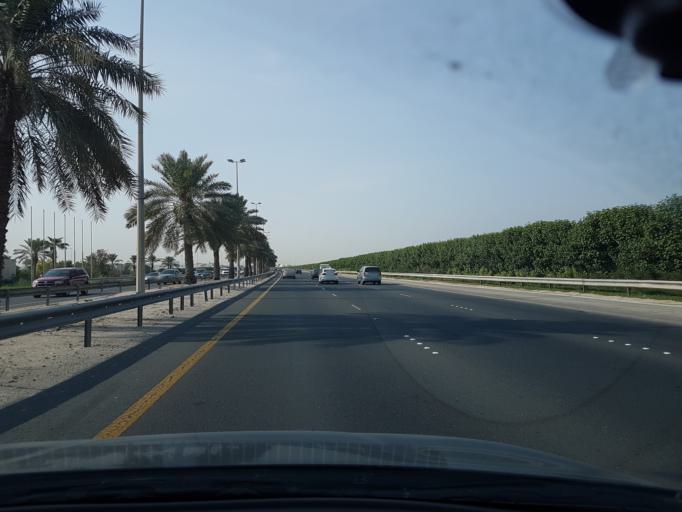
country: BH
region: Northern
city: Madinat `Isa
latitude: 26.1656
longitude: 50.5034
